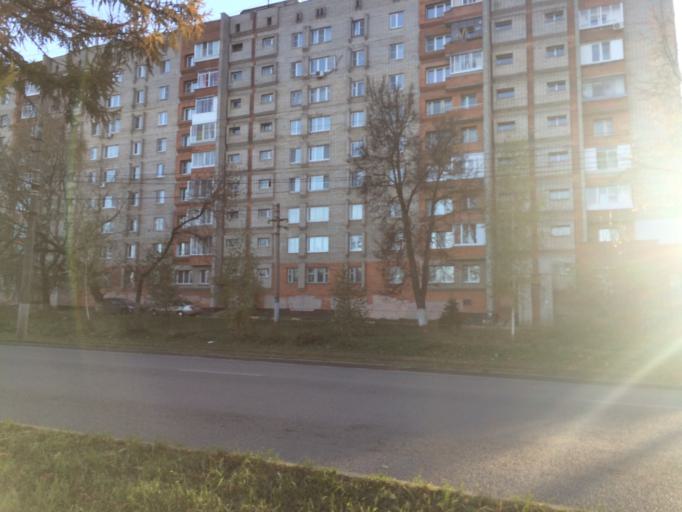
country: RU
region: Tula
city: Mendeleyevskiy
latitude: 54.1660
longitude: 37.5910
